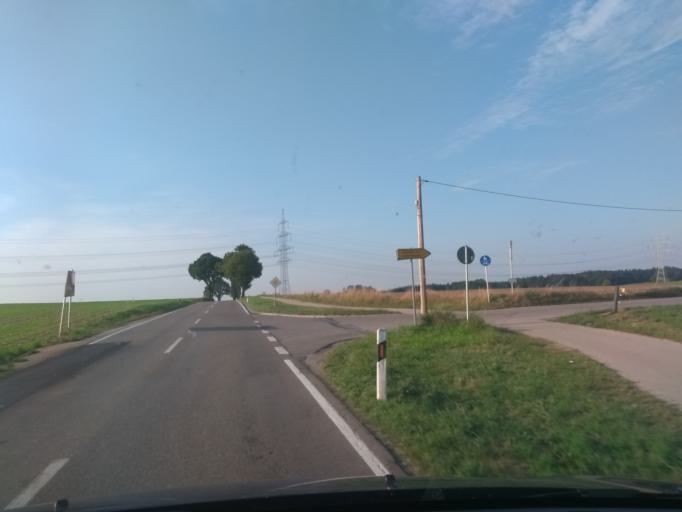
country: DE
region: Bavaria
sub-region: Upper Bavaria
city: Schwabhausen
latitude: 48.2978
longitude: 11.3964
